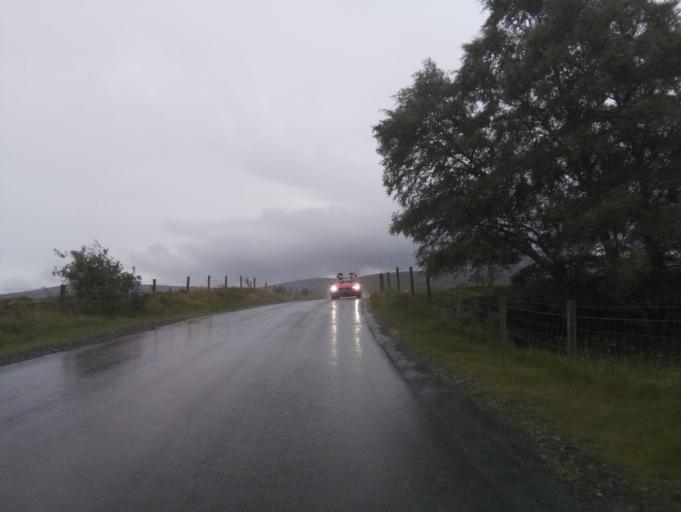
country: GB
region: Scotland
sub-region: Highland
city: Grantown on Spey
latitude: 57.3024
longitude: -3.5640
